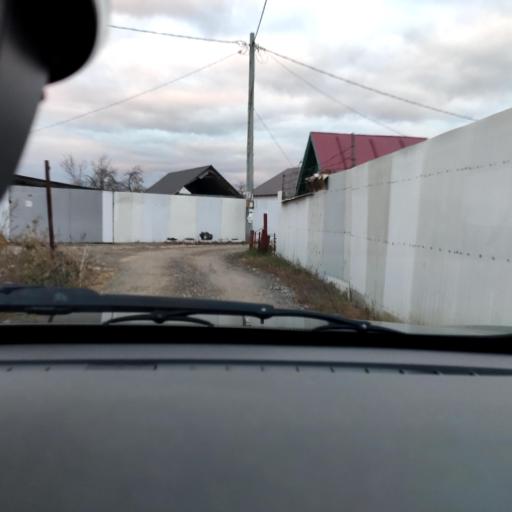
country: RU
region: Samara
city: Tol'yatti
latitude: 53.5412
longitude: 49.4297
